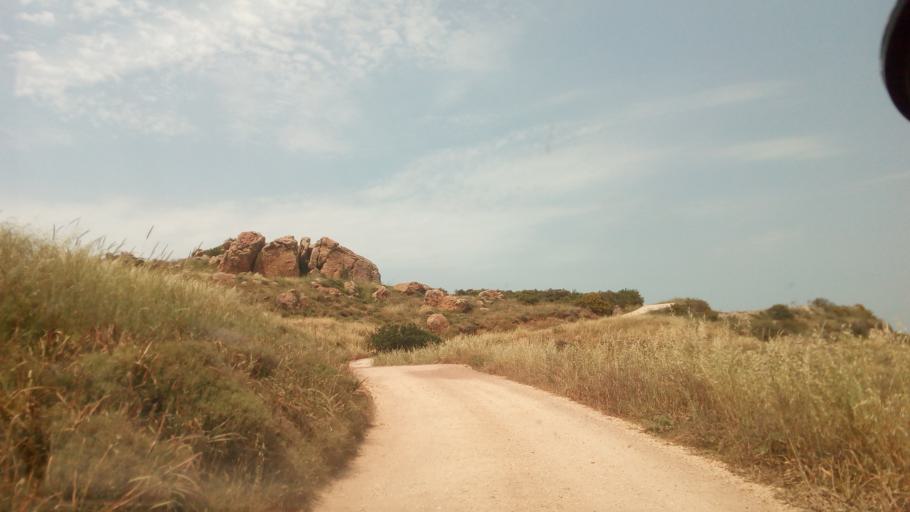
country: CY
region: Pafos
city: Polis
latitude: 34.9813
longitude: 32.3551
